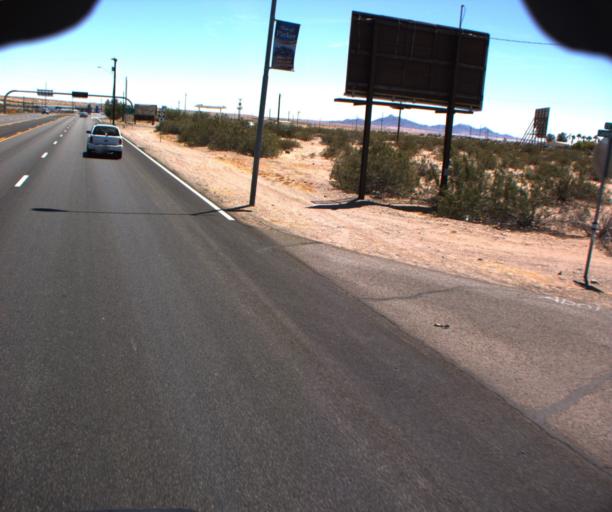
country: US
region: Arizona
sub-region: La Paz County
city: Parker
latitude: 34.1406
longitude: -114.2831
